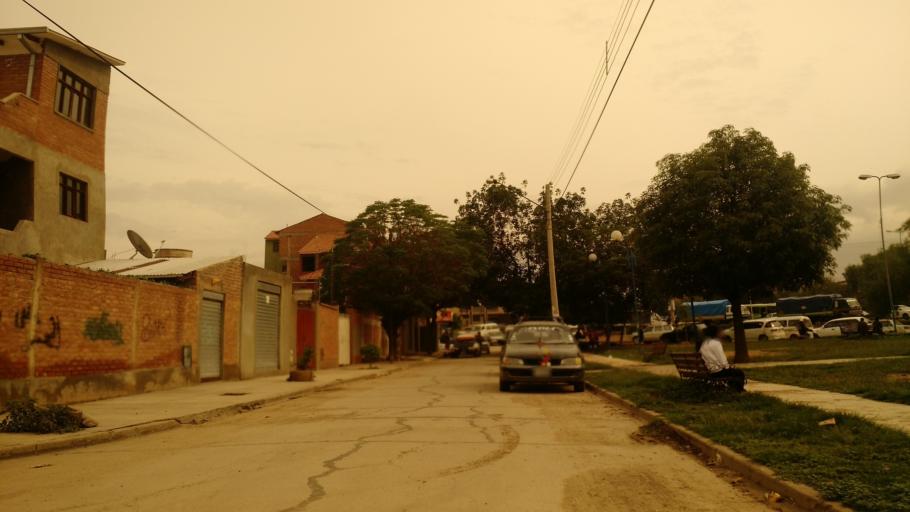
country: BO
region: Cochabamba
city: Cochabamba
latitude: -17.4302
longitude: -66.1560
